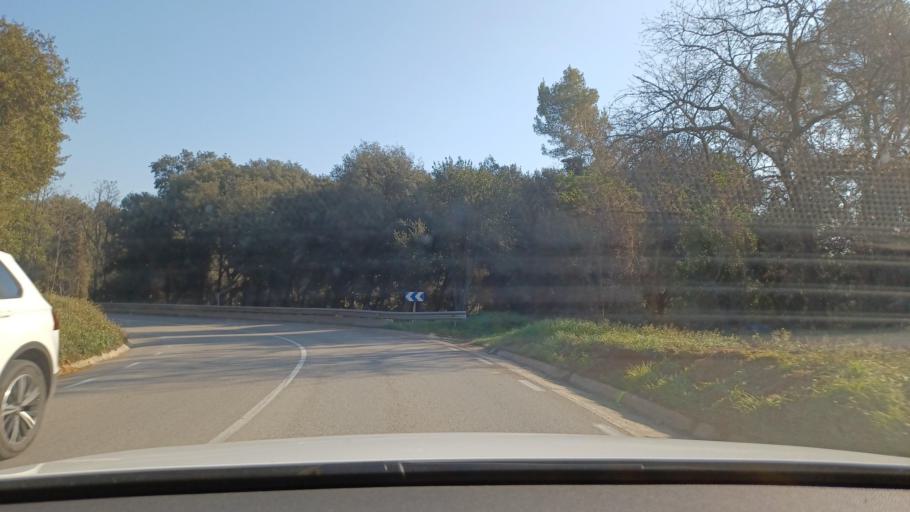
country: ES
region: Catalonia
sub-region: Provincia de Barcelona
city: L'Ametlla del Valles
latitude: 41.6633
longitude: 2.2511
